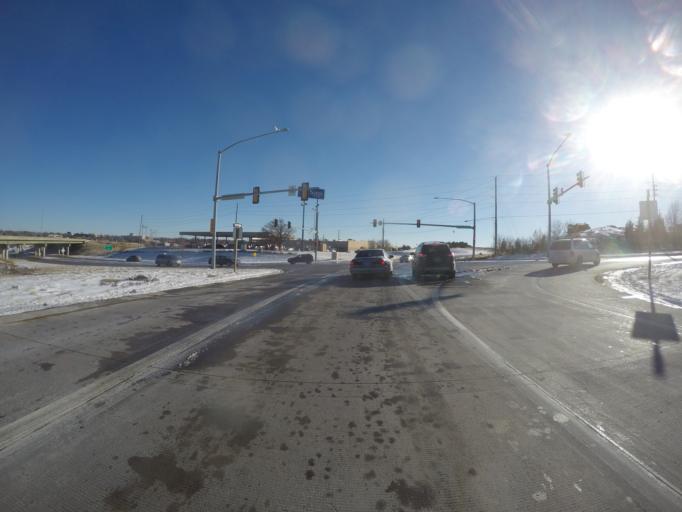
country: US
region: Kansas
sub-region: Shawnee County
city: Topeka
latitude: 39.0438
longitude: -95.7660
